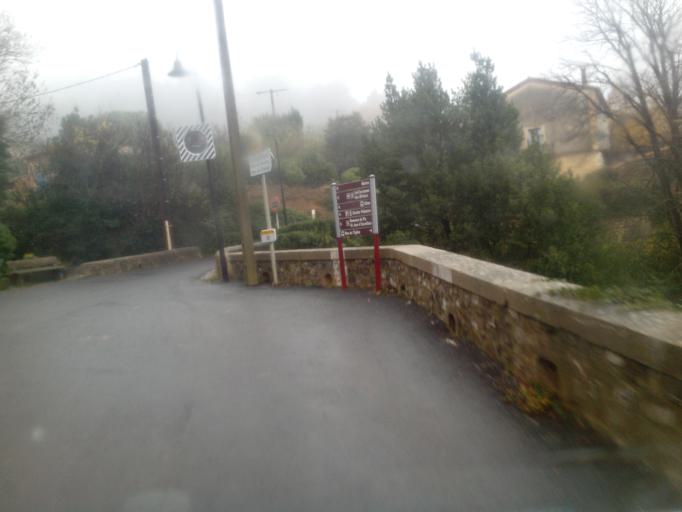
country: FR
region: Languedoc-Roussillon
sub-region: Departement de l'Herault
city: Nebian
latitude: 43.6351
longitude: 3.3722
